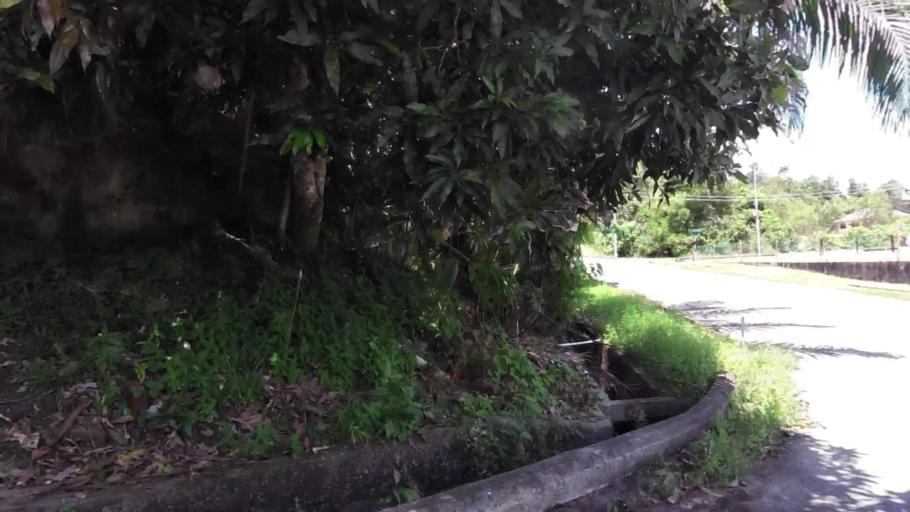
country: BN
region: Brunei and Muara
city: Bandar Seri Begawan
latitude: 4.9353
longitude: 114.9701
